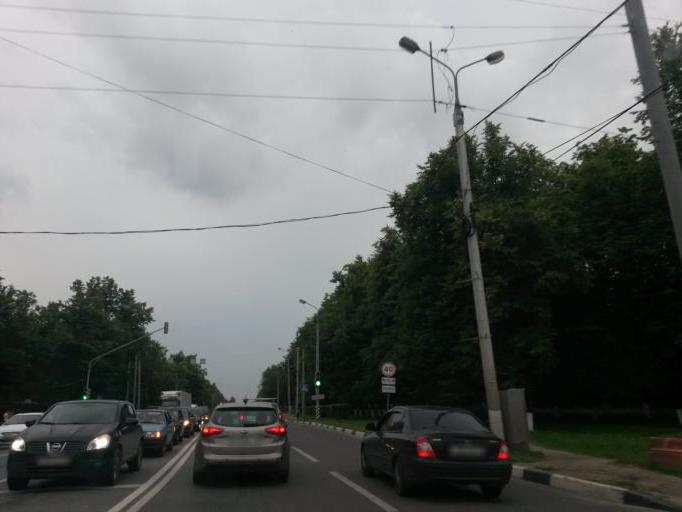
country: RU
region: Moskovskaya
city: Domodedovo
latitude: 55.4285
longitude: 37.7705
